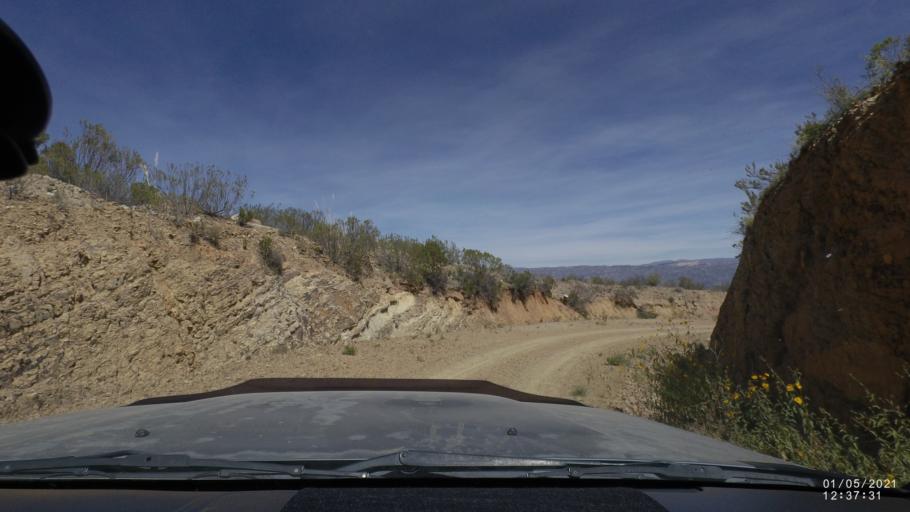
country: BO
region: Cochabamba
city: Capinota
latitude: -17.6793
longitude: -66.1569
